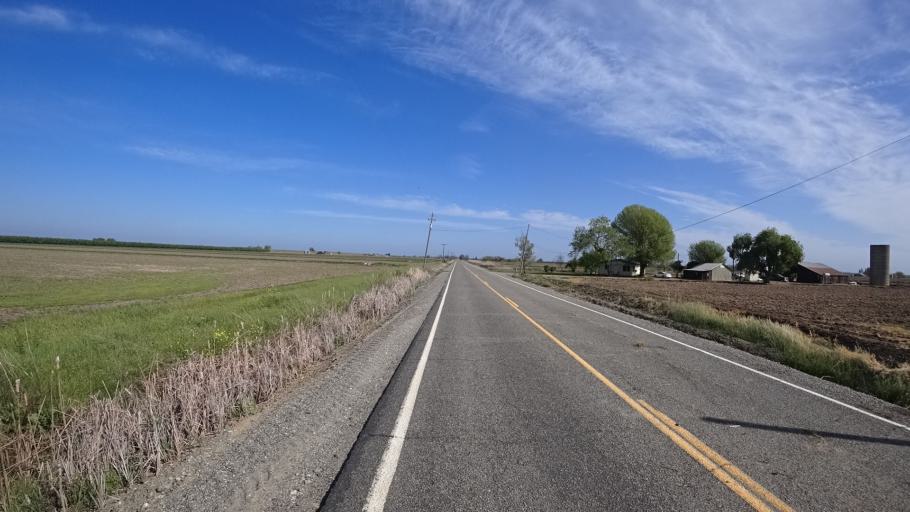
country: US
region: California
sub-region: Glenn County
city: Hamilton City
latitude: 39.6089
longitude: -122.0370
